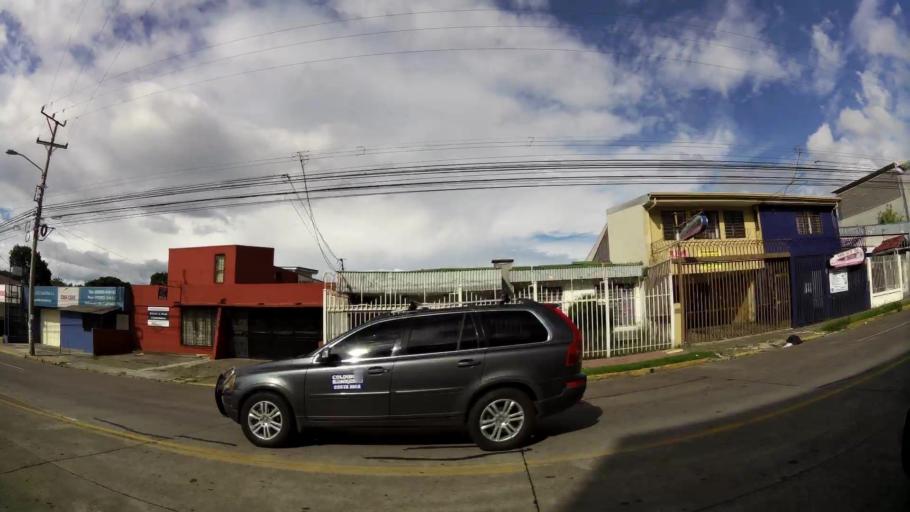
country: CR
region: San Jose
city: San Rafael
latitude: 9.9441
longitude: -84.1285
